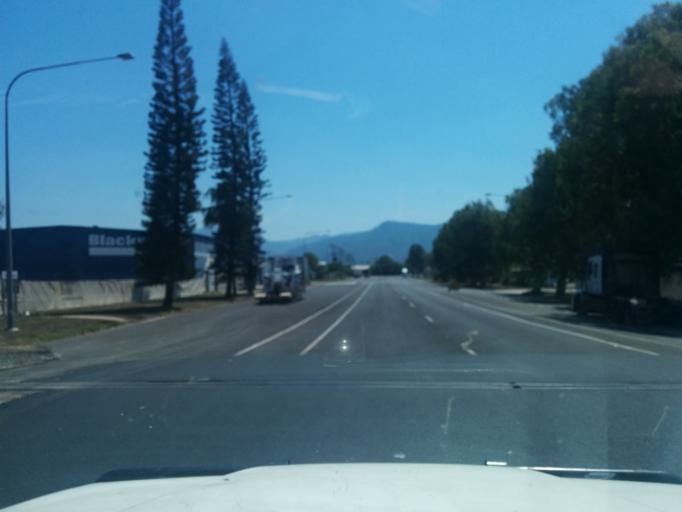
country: AU
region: Queensland
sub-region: Cairns
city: Cairns
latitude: -16.9411
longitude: 145.7732
